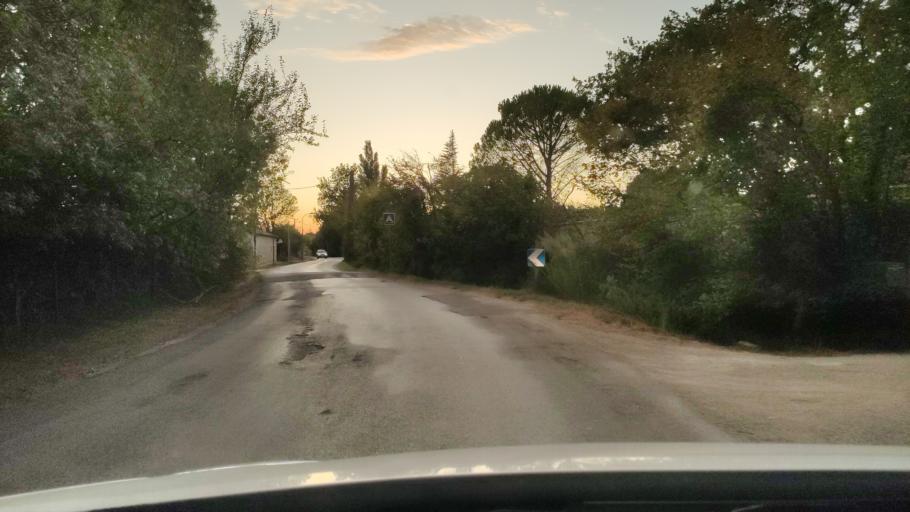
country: FR
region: Provence-Alpes-Cote d'Azur
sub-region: Departement du Vaucluse
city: Velleron
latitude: 43.9589
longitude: 5.0385
